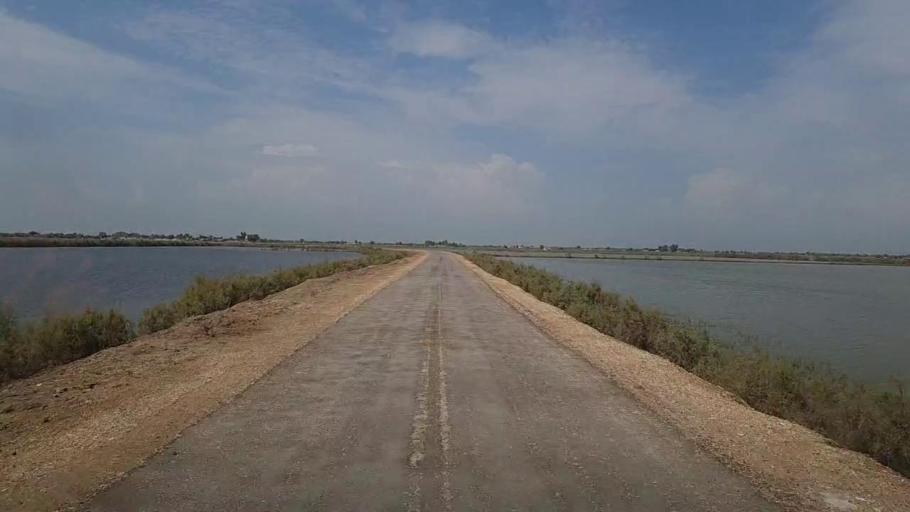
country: PK
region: Sindh
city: Thul
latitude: 28.2819
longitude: 68.8227
